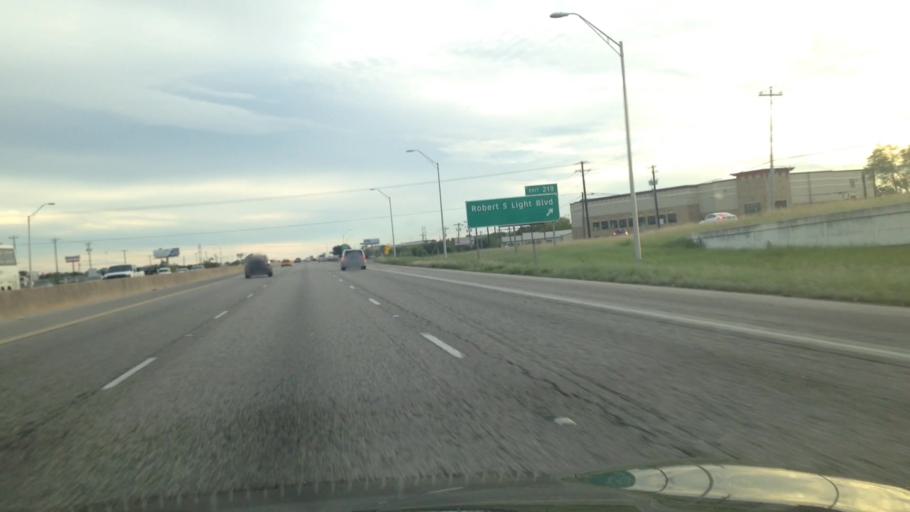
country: US
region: Texas
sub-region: Hays County
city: Buda
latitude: 30.0781
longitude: -97.8247
